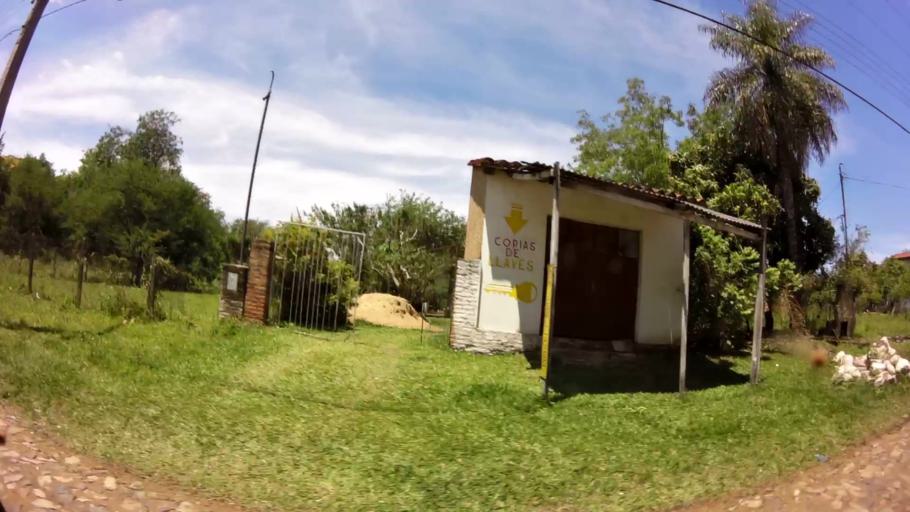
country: PY
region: Central
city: Colonia Mariano Roque Alonso
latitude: -25.1976
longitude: -57.5491
